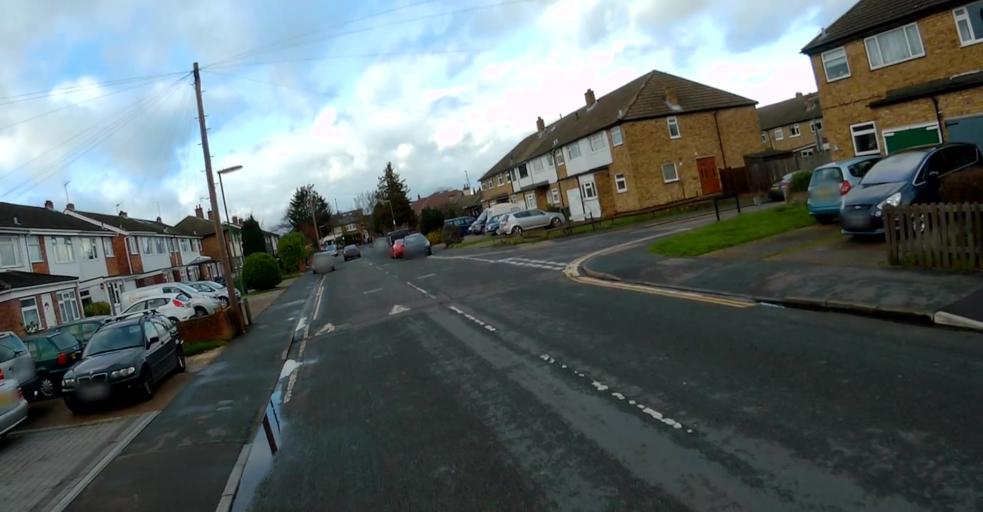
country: GB
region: England
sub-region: Surrey
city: Walton-on-Thames
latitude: 51.3881
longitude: -0.4146
